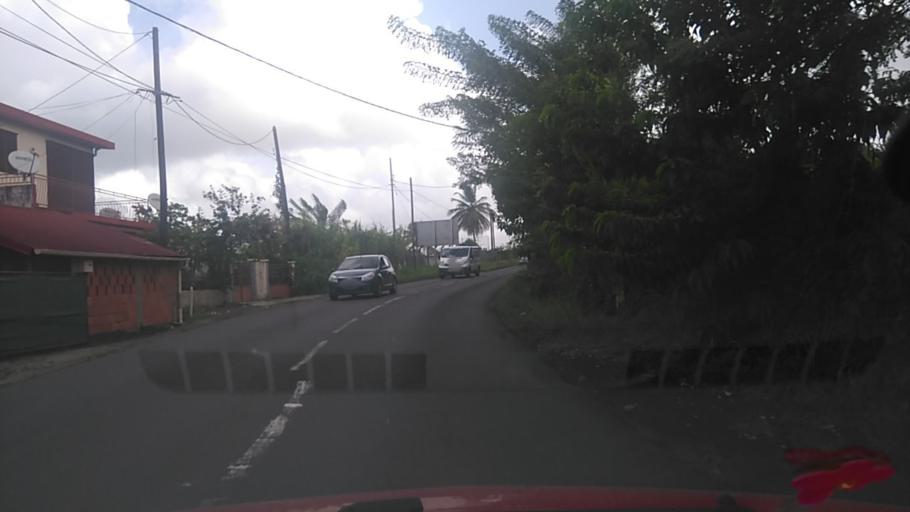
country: MQ
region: Martinique
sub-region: Martinique
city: Le Lamentin
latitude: 14.6241
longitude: -60.9893
